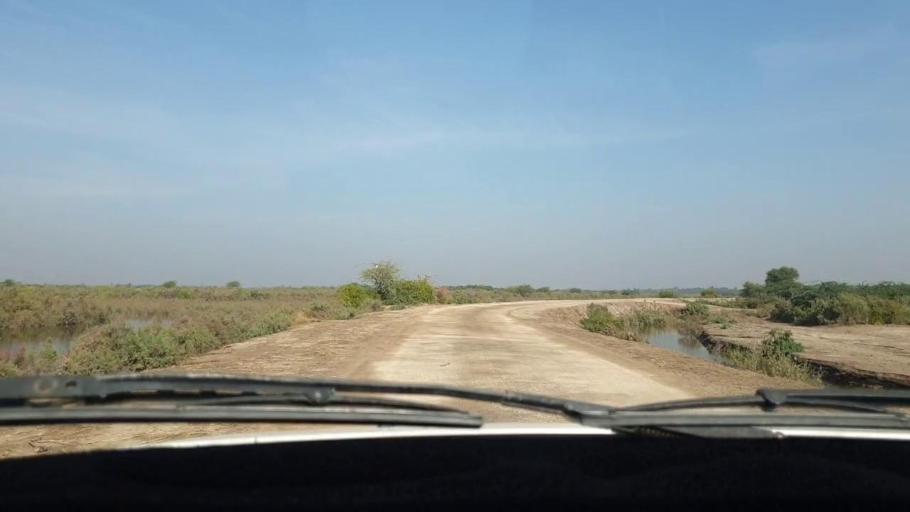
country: PK
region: Sindh
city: Tando Muhammad Khan
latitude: 24.9862
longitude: 68.4620
